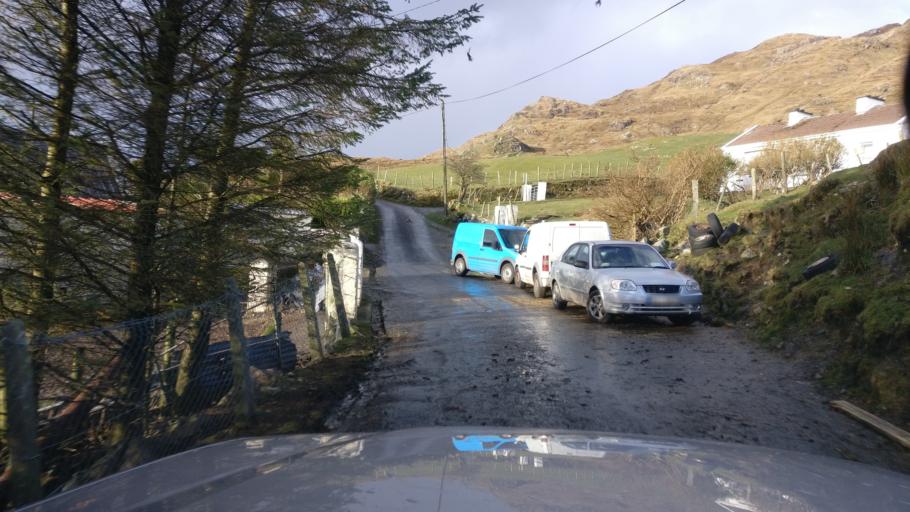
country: IE
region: Connaught
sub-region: County Galway
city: Clifden
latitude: 53.4772
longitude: -9.7256
